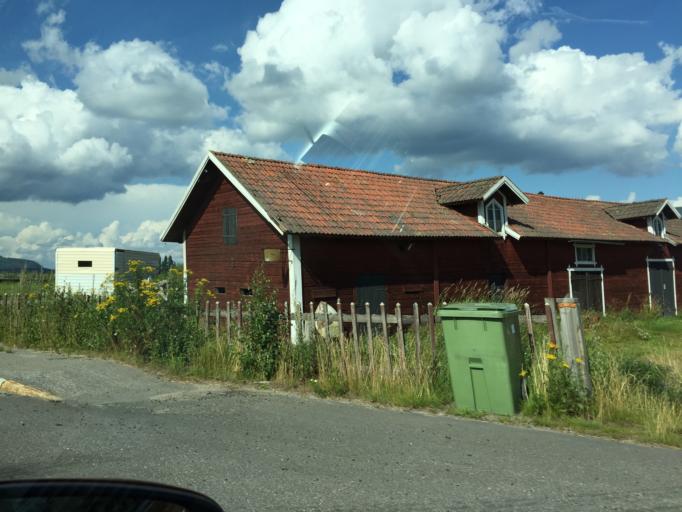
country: SE
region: Gaevleborg
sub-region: Bollnas Kommun
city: Arbra
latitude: 61.4977
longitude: 16.3644
